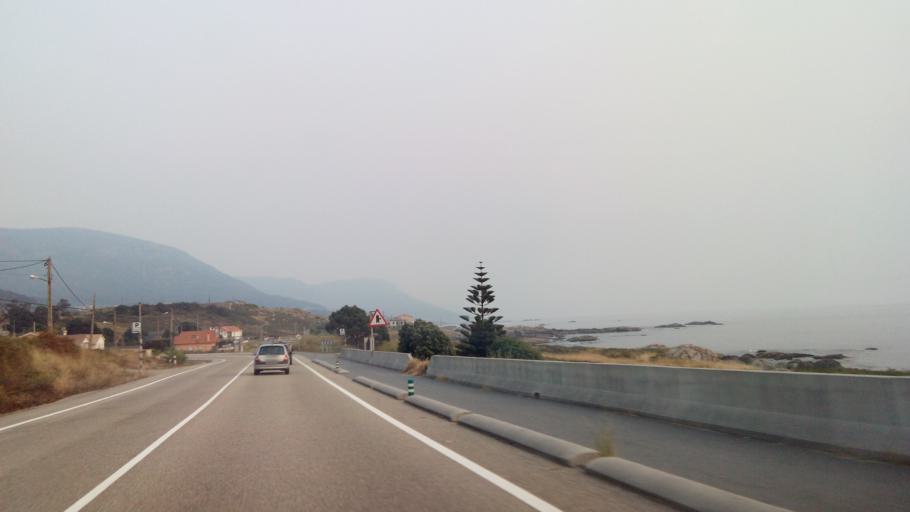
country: ES
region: Galicia
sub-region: Provincia de Pontevedra
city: Oia
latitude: 42.0587
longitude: -8.8895
